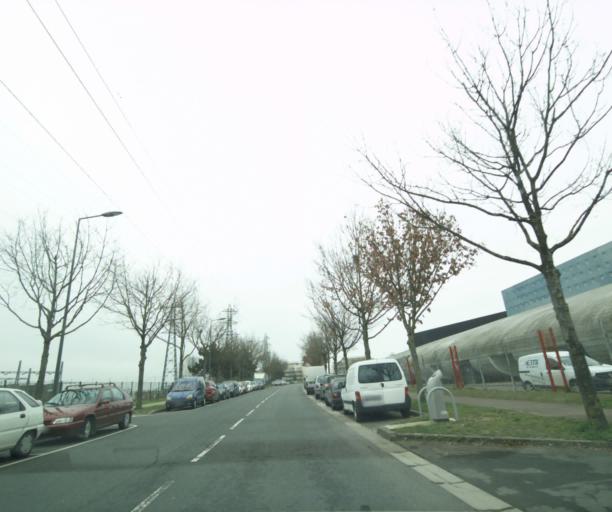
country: FR
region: Ile-de-France
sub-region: Departement du Val-d'Oise
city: Courdimanche
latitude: 49.0530
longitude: 2.0110
